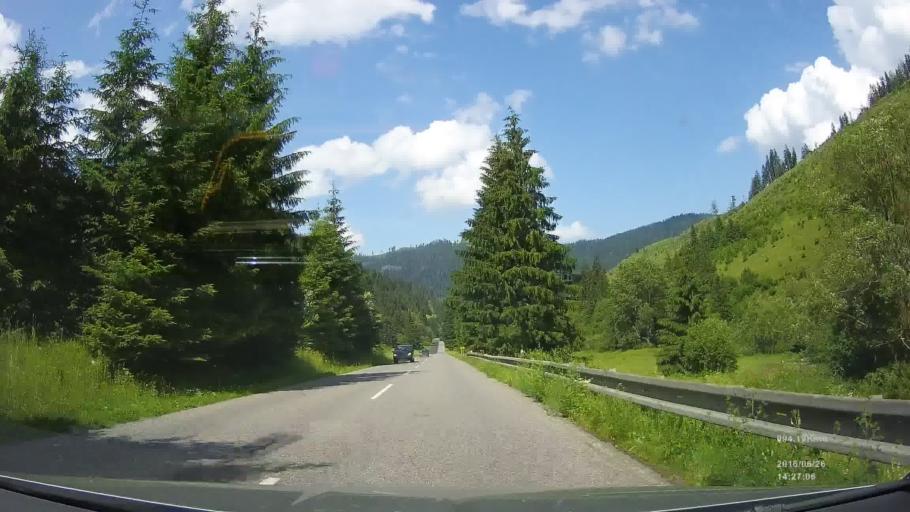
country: SK
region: Zilinsky
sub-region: Okres Zilina
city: Liptovsky Hradok
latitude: 48.9610
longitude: 19.7739
